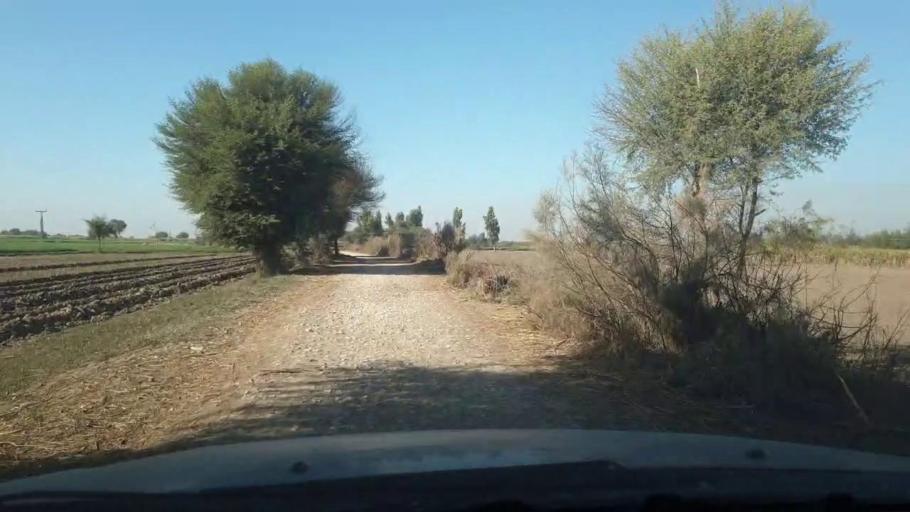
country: PK
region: Sindh
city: Pano Aqil
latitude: 27.9766
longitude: 69.1715
